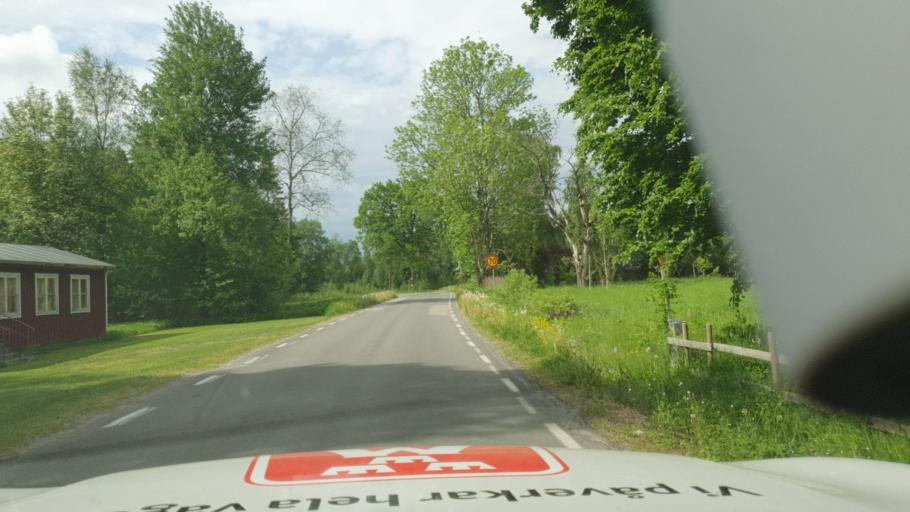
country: SE
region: Vaestra Goetaland
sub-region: Falkopings Kommun
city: Floby
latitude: 57.9881
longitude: 13.4052
